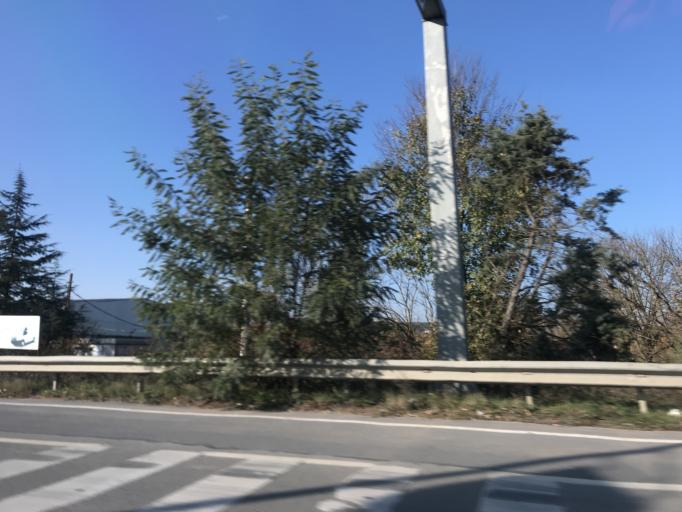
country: TR
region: Istanbul
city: Sultanbeyli
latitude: 40.9332
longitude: 29.3430
